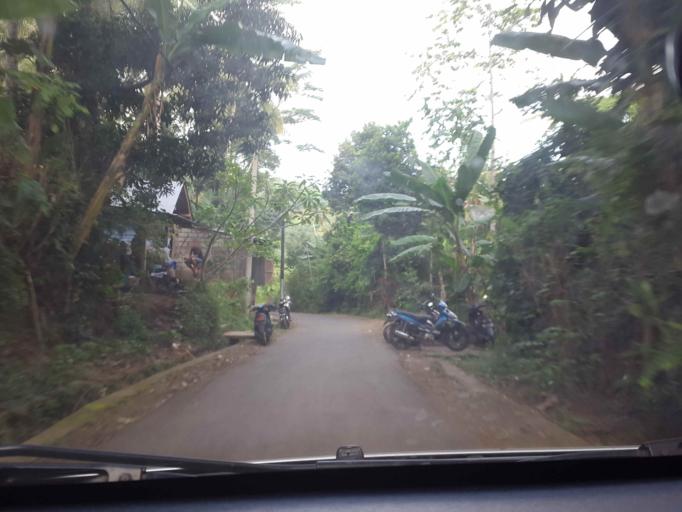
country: ID
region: Bali
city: Semarapura
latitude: -8.5349
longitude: 115.4196
